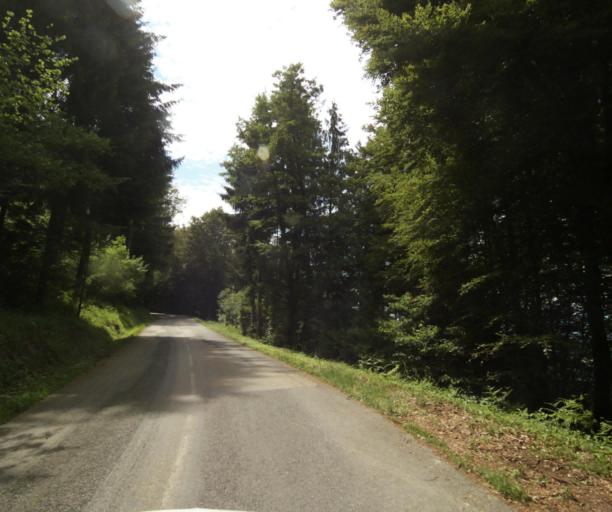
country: FR
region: Rhone-Alpes
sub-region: Departement de la Haute-Savoie
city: Perrignier
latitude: 46.3004
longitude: 6.4730
